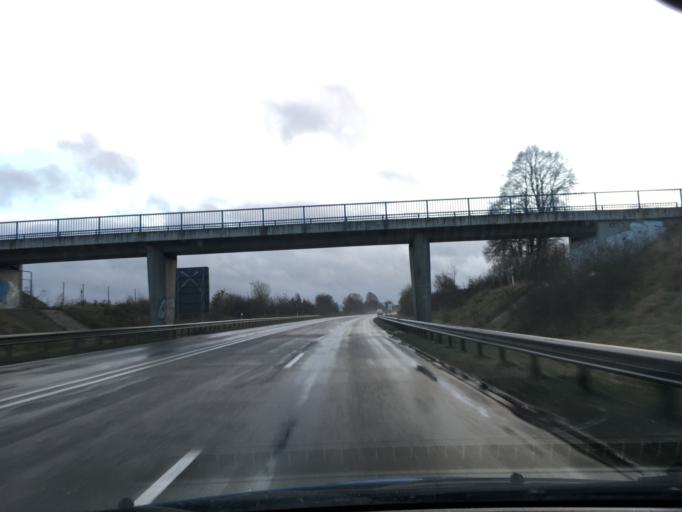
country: DE
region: Lower Saxony
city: Uelzen
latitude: 52.9560
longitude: 10.5897
